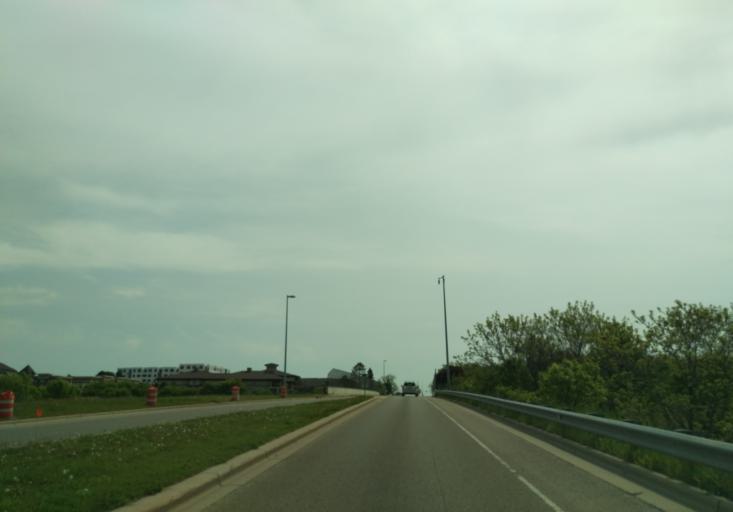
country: US
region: Wisconsin
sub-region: Dane County
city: Monona
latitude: 43.0844
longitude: -89.2850
